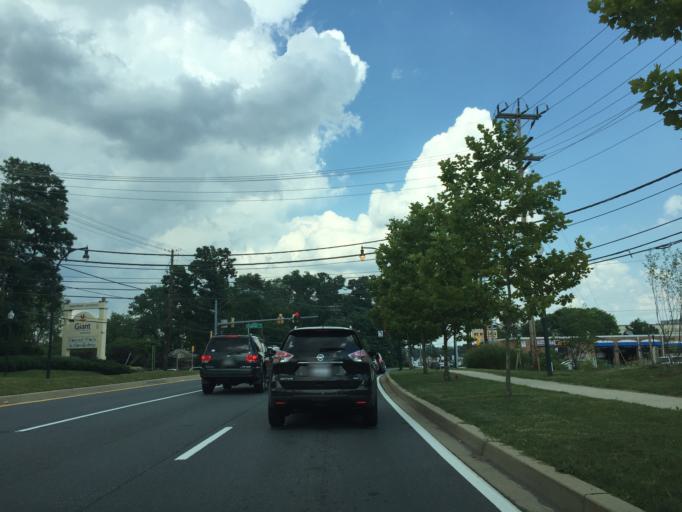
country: US
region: Maryland
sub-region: Montgomery County
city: North Bethesda
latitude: 39.0530
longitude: -77.1145
